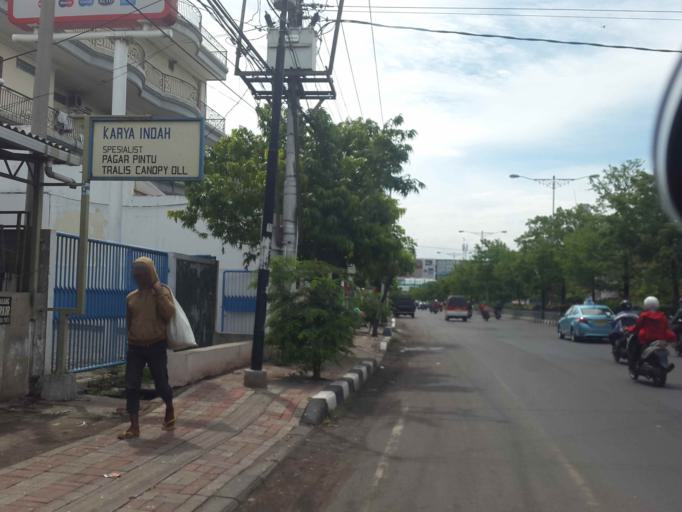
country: ID
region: Central Java
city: Semarang
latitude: -6.9809
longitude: 110.3993
